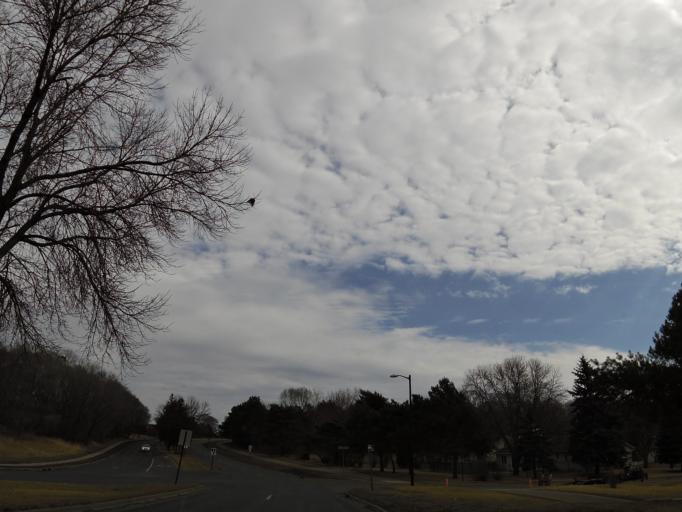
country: US
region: Minnesota
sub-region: Scott County
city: Savage
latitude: 44.8186
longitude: -93.3922
